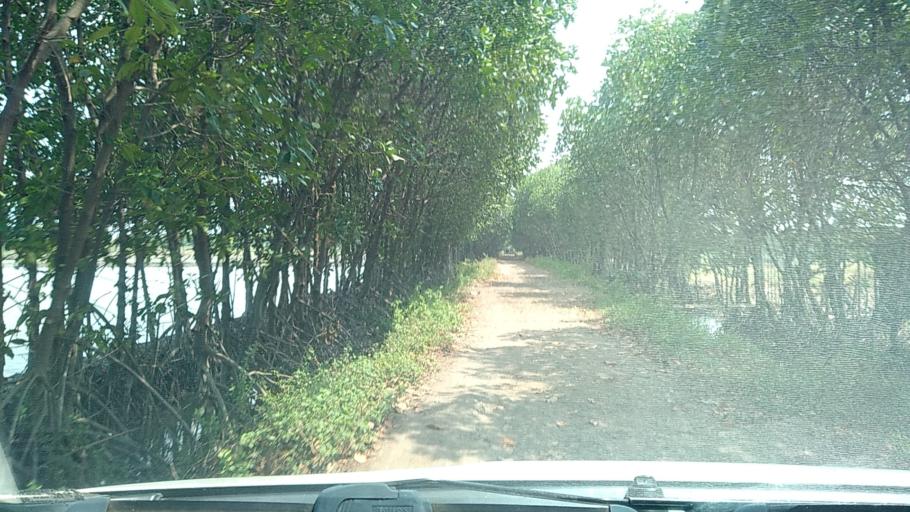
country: ID
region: Central Java
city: Semarang
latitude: -6.9739
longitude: 110.3531
